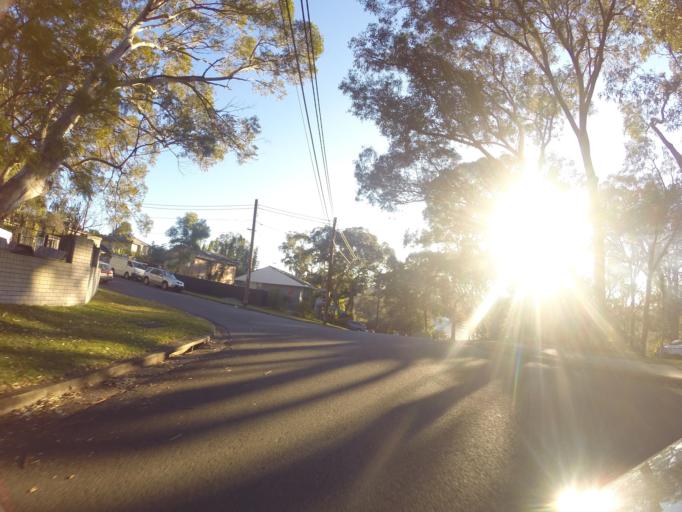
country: AU
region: New South Wales
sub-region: Sutherland Shire
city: Grays Point
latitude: -34.0591
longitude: 151.0801
